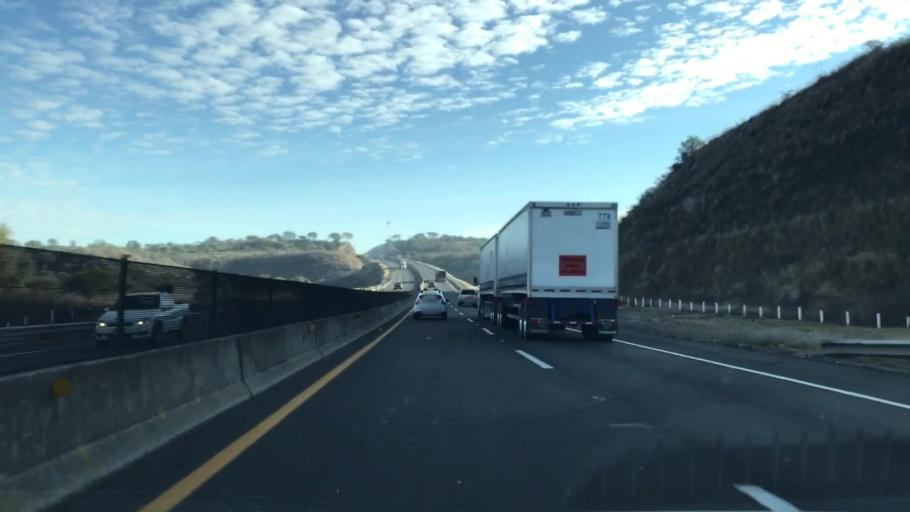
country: MX
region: Jalisco
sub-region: San Juan de los Lagos
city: Mezquitic de la Magdalena
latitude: 21.1914
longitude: -102.3501
